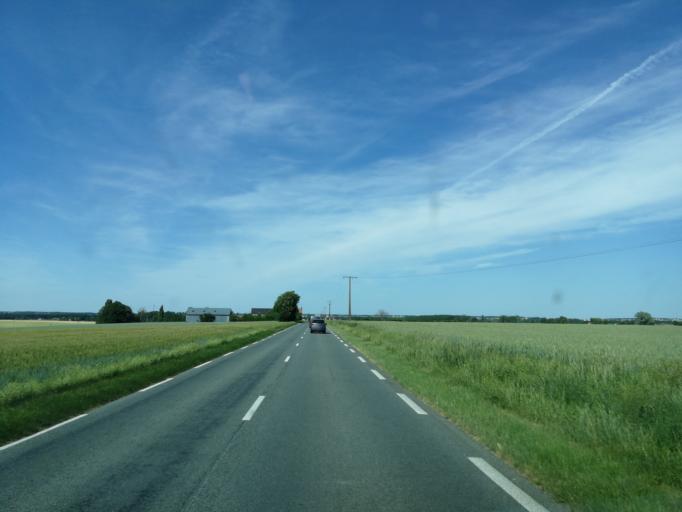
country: FR
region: Poitou-Charentes
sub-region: Departement de la Vienne
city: Loudun
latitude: 47.0691
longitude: 0.1680
